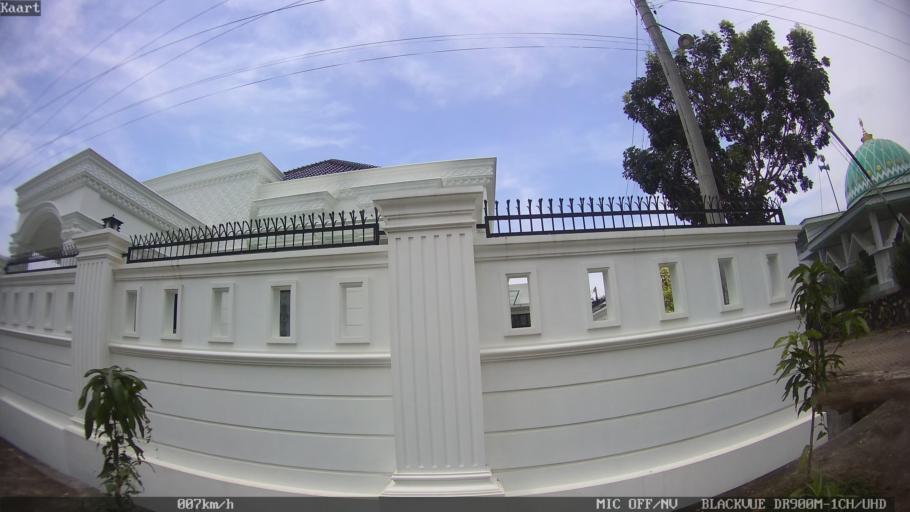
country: ID
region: Lampung
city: Bandarlampung
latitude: -5.4066
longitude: 105.2017
